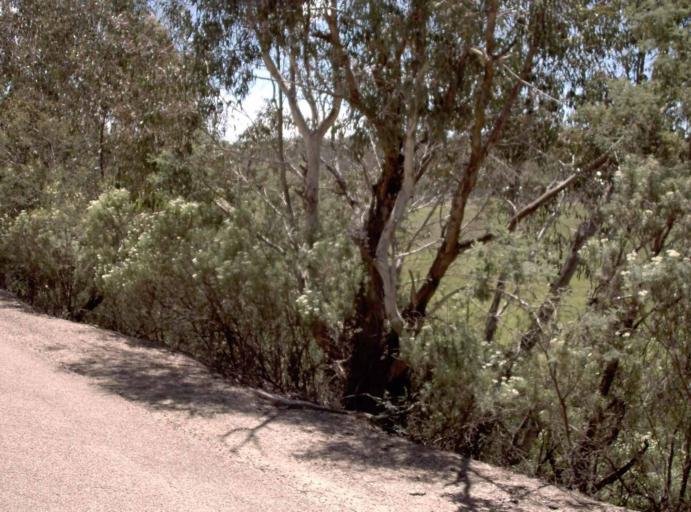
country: AU
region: New South Wales
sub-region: Snowy River
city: Jindabyne
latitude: -37.0470
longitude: 148.2766
